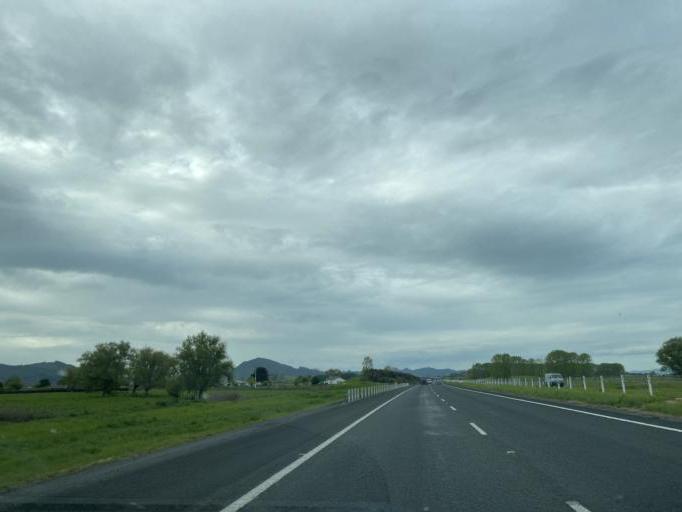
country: NZ
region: Waikato
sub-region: Waikato District
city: Ngaruawahia
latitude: -37.6558
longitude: 175.2056
